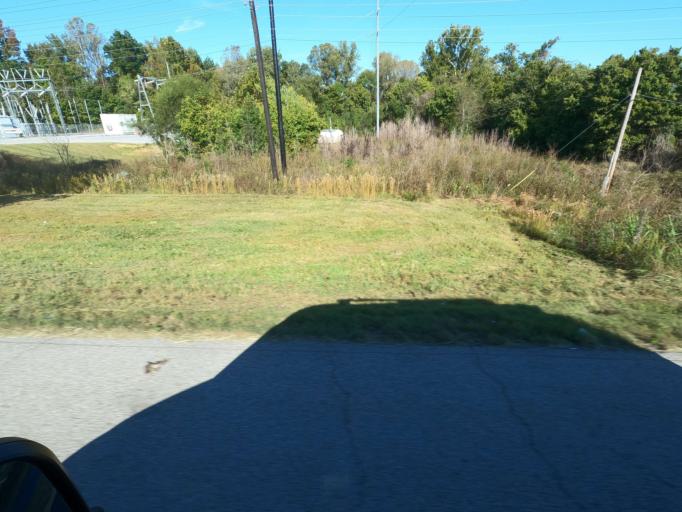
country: US
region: Tennessee
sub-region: Tipton County
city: Brighton
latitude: 35.4920
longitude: -89.7264
